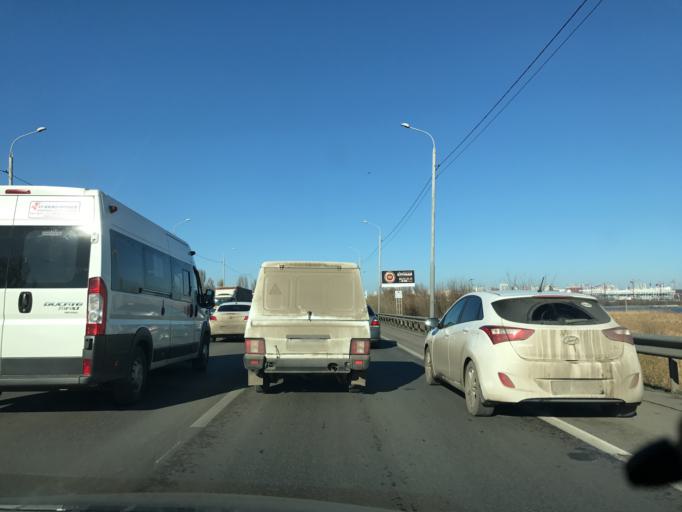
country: RU
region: Rostov
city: Rostov-na-Donu
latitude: 47.1913
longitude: 39.7344
